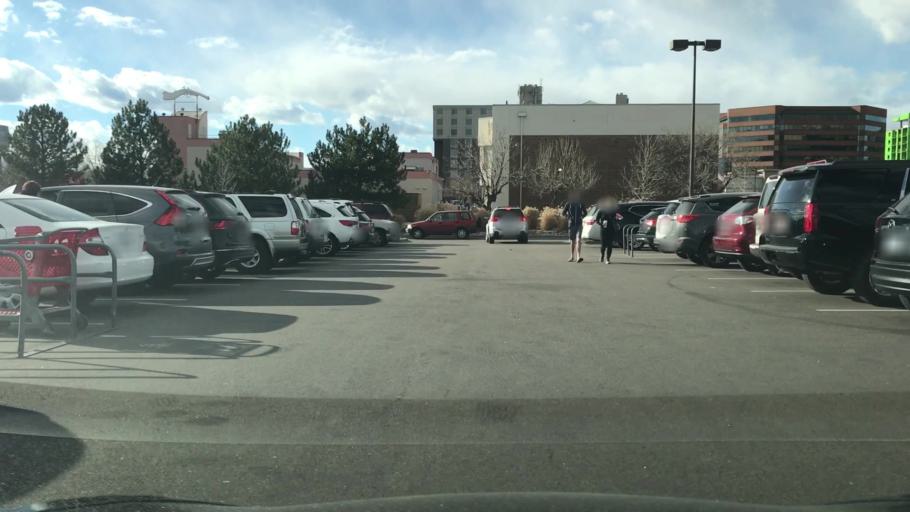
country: US
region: Colorado
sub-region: Arapahoe County
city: Glendale
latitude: 39.7079
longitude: -104.9385
